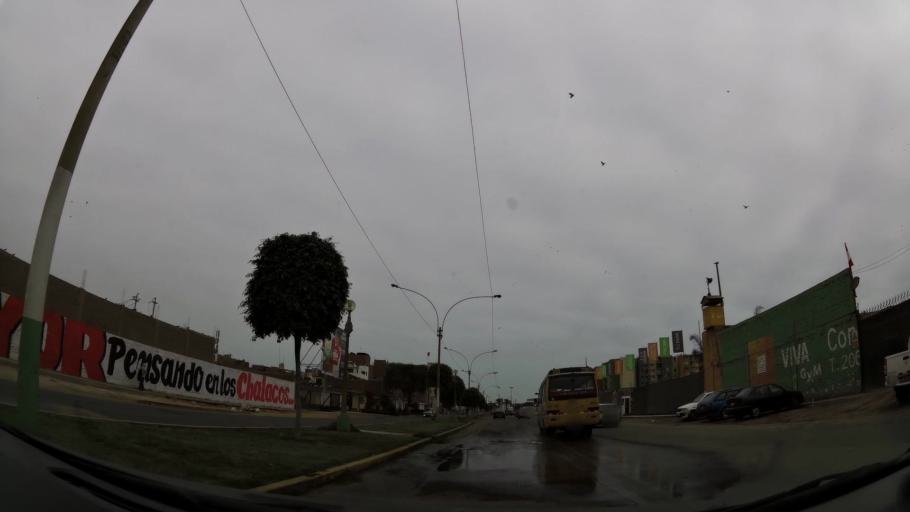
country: PE
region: Callao
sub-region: Callao
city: Callao
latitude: -12.0506
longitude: -77.1153
